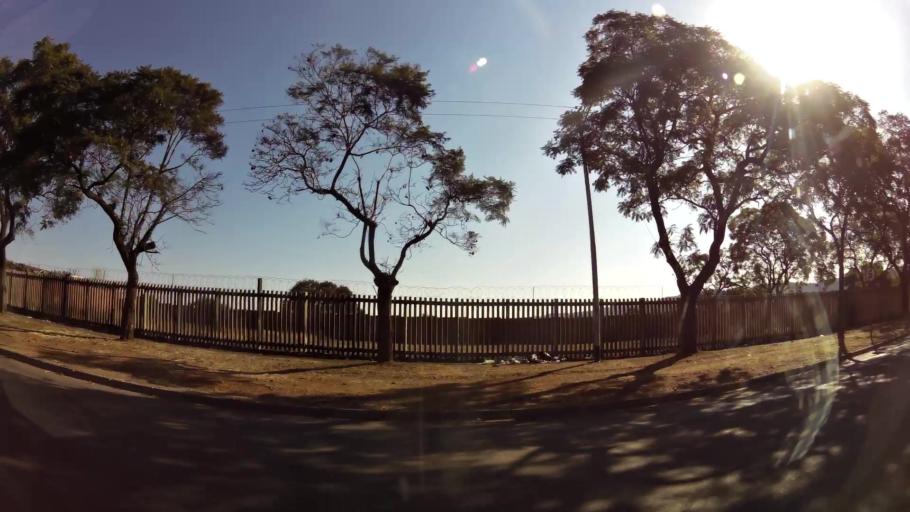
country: ZA
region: Gauteng
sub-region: City of Tshwane Metropolitan Municipality
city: Pretoria
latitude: -25.7400
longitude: 28.1717
